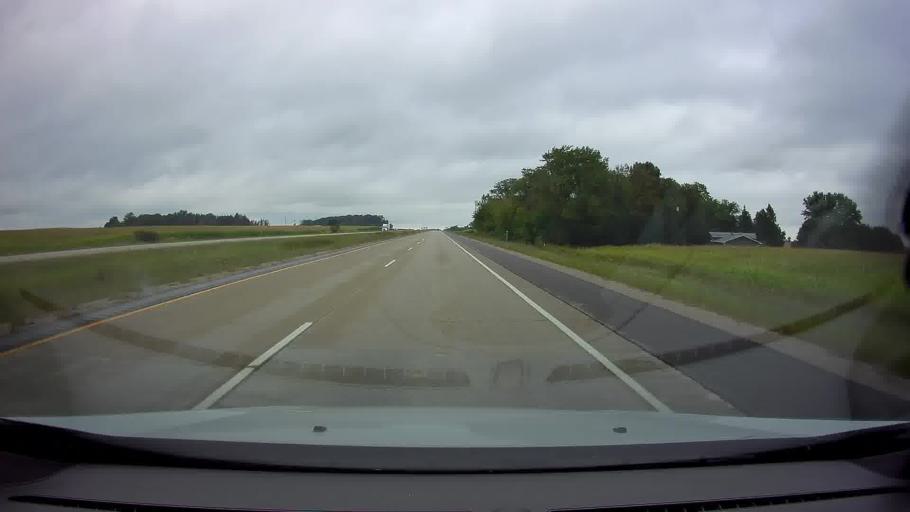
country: US
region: Wisconsin
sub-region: Brown County
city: Pulaski
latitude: 44.6399
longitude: -88.2876
